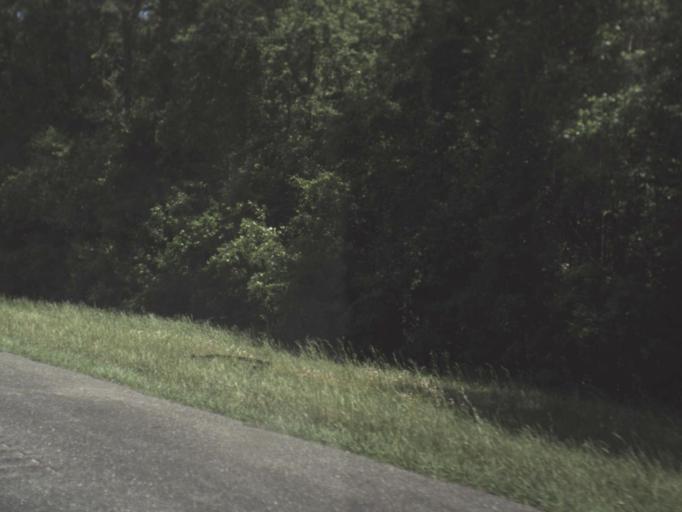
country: US
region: Florida
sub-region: Jefferson County
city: Monticello
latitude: 30.4784
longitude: -83.9326
